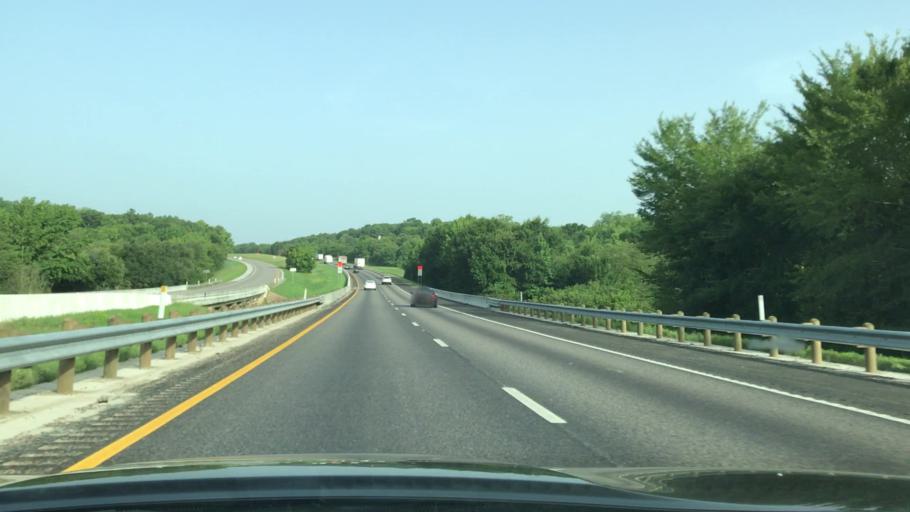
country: US
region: Texas
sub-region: Smith County
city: Lindale
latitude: 32.4671
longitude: -95.3397
